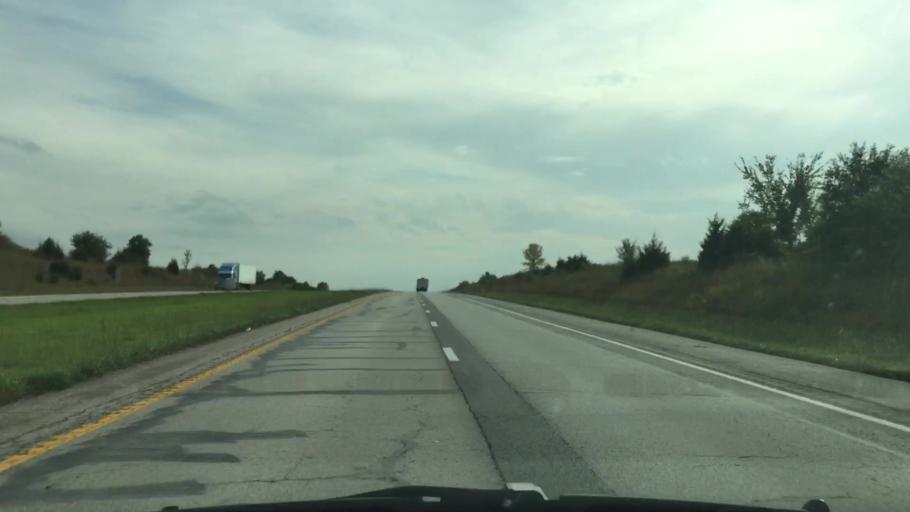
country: US
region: Missouri
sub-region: Harrison County
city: Bethany
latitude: 40.4234
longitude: -93.9892
